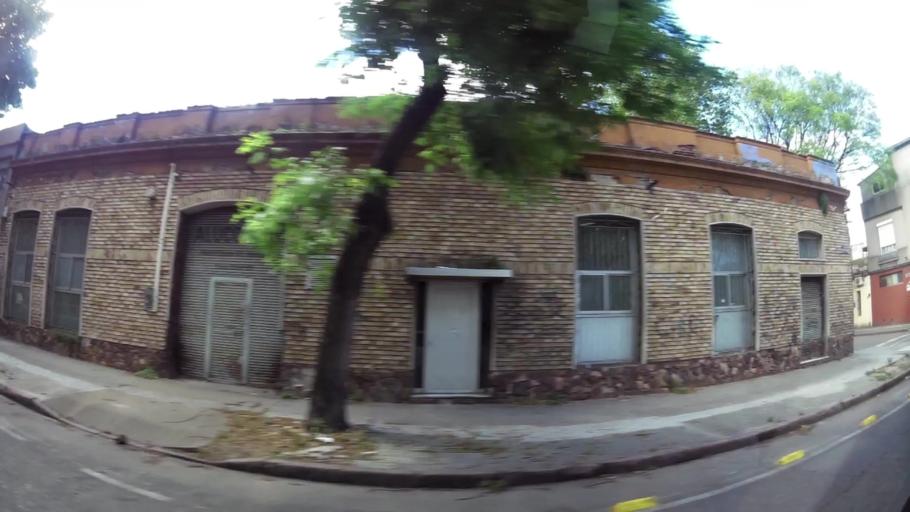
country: UY
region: Montevideo
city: Montevideo
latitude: -34.8893
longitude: -56.1800
